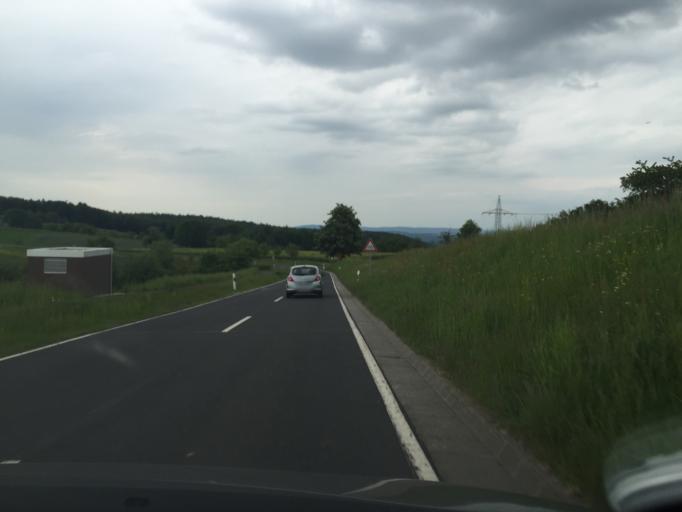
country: DE
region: Bavaria
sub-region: Regierungsbezirk Unterfranken
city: Johannesberg
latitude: 50.0357
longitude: 9.1137
